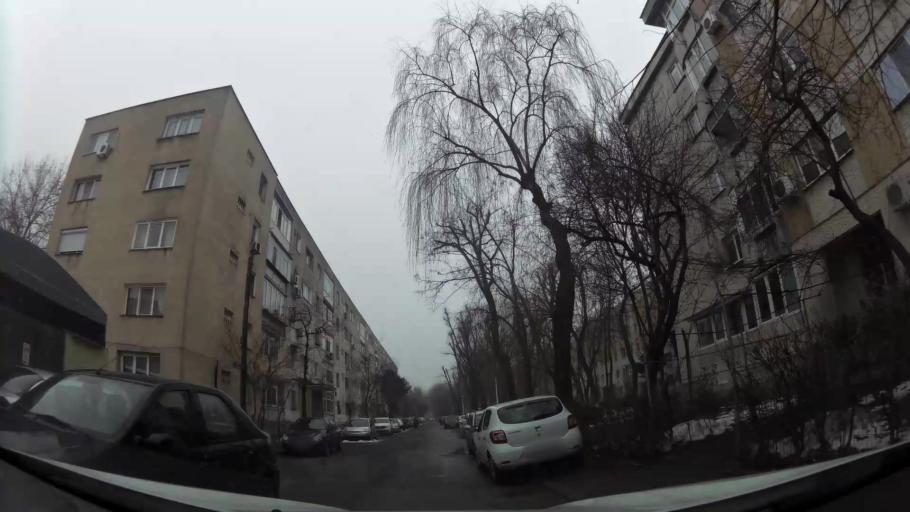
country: RO
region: Ilfov
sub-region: Comuna Chiajna
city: Rosu
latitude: 44.4402
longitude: 26.0200
